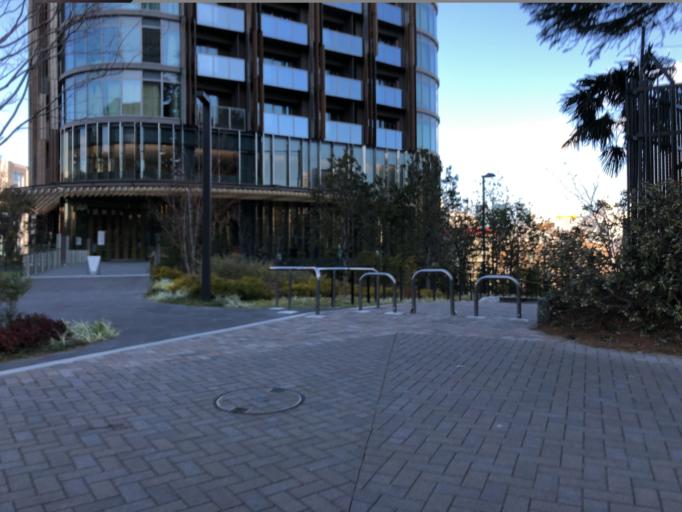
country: JP
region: Tokyo
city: Tokyo
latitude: 35.6678
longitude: 139.7303
